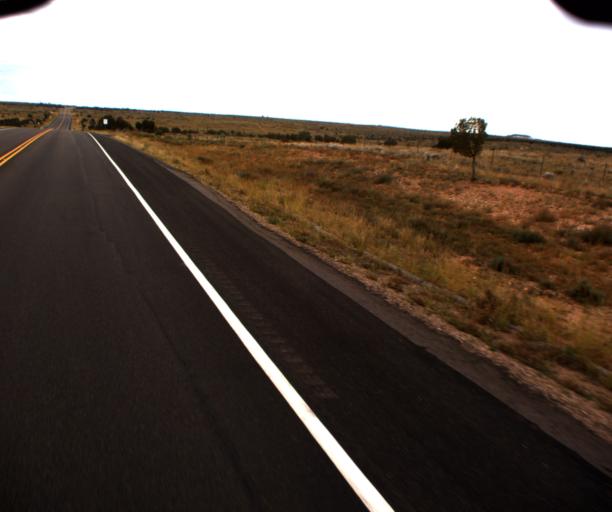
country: US
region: Arizona
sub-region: Navajo County
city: Snowflake
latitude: 34.5960
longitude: -110.0874
